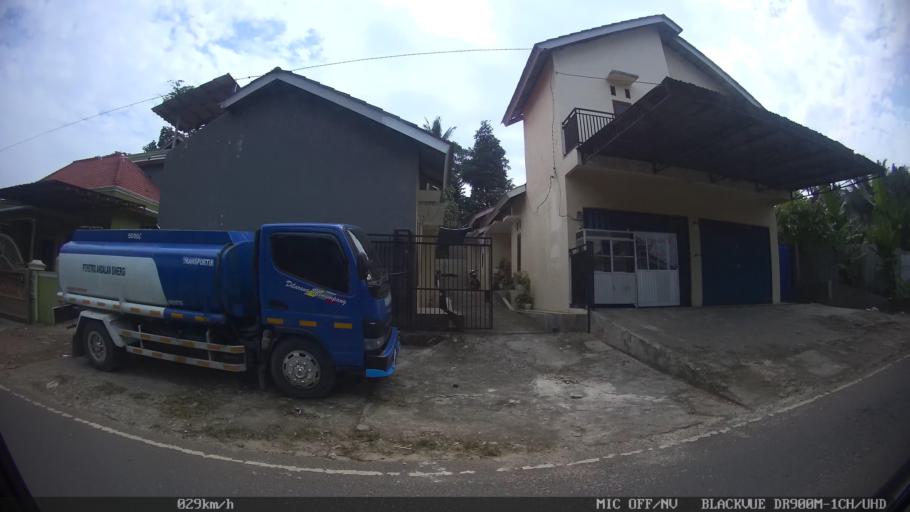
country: ID
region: Lampung
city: Bandarlampung
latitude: -5.4421
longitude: 105.2411
